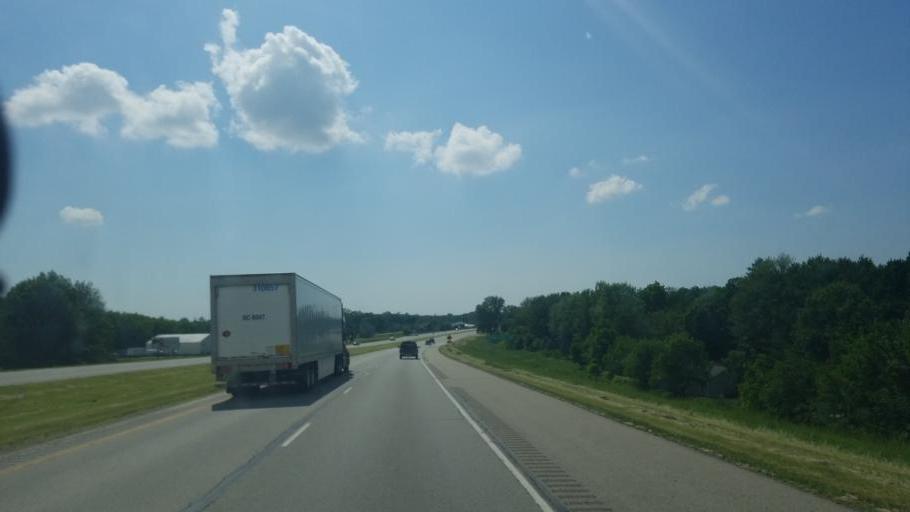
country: US
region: Indiana
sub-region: Kosciusko County
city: Mentone
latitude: 41.2650
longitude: -85.9842
